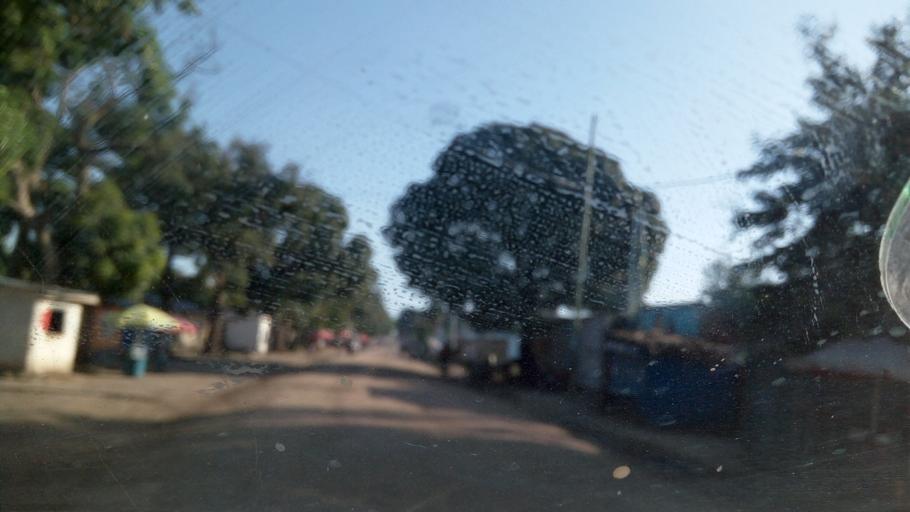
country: BI
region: Bururi
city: Rumonge
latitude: -4.1060
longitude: 29.0920
